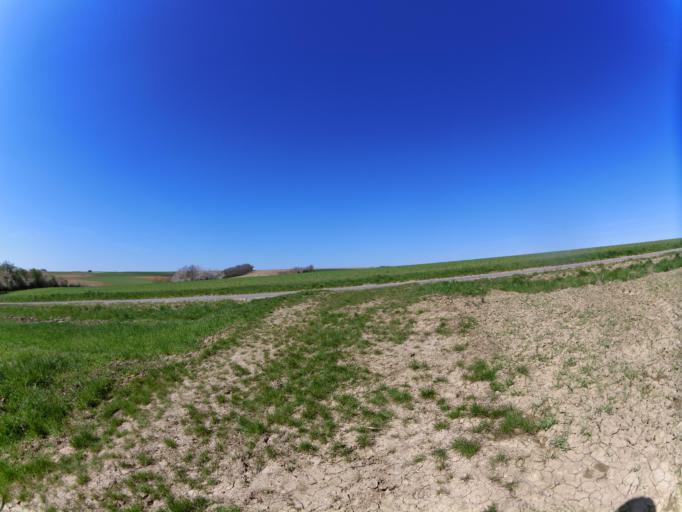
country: DE
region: Bavaria
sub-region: Regierungsbezirk Unterfranken
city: Winterhausen
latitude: 49.6893
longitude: 9.9950
